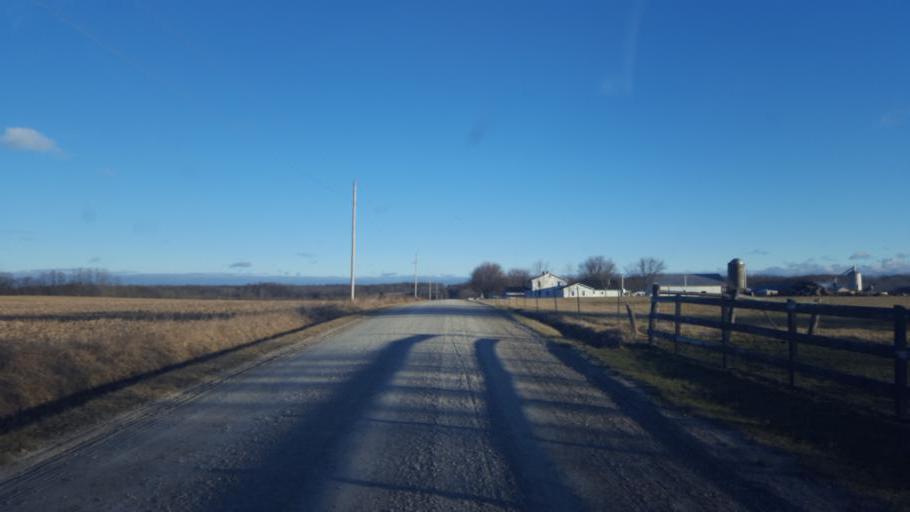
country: US
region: Ohio
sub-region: Knox County
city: Fredericktown
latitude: 40.5504
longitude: -82.6428
